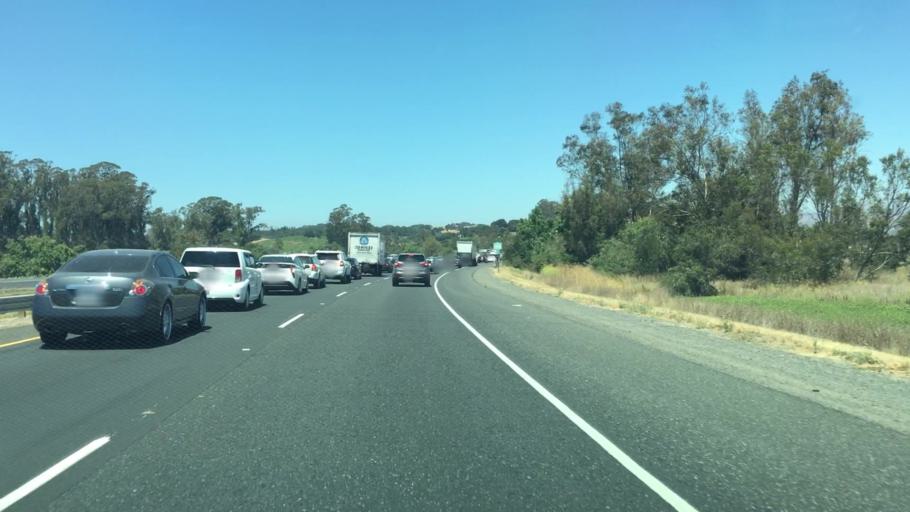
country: US
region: California
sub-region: Napa County
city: Napa
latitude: 38.2517
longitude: -122.3035
